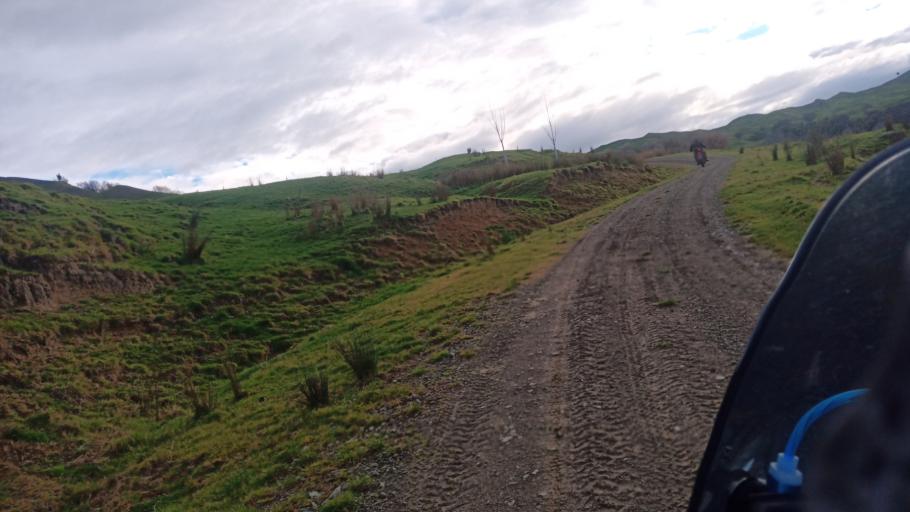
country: NZ
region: Gisborne
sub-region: Gisborne District
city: Gisborne
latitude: -38.3484
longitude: 177.9334
